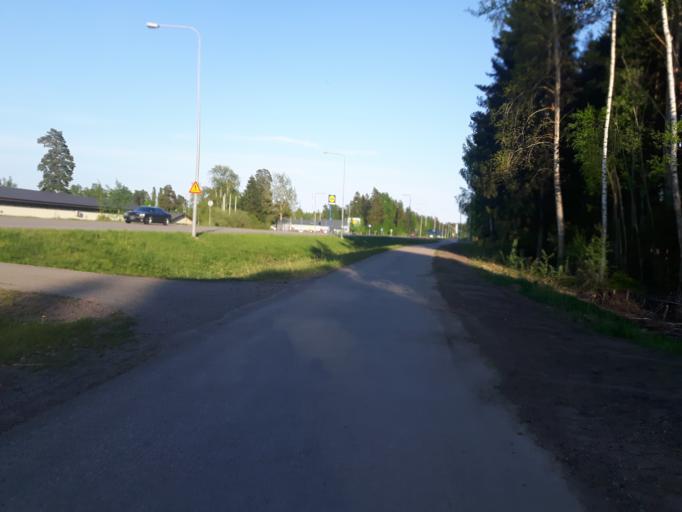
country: FI
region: Uusimaa
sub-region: Loviisa
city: Lovisa
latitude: 60.4575
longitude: 26.1959
